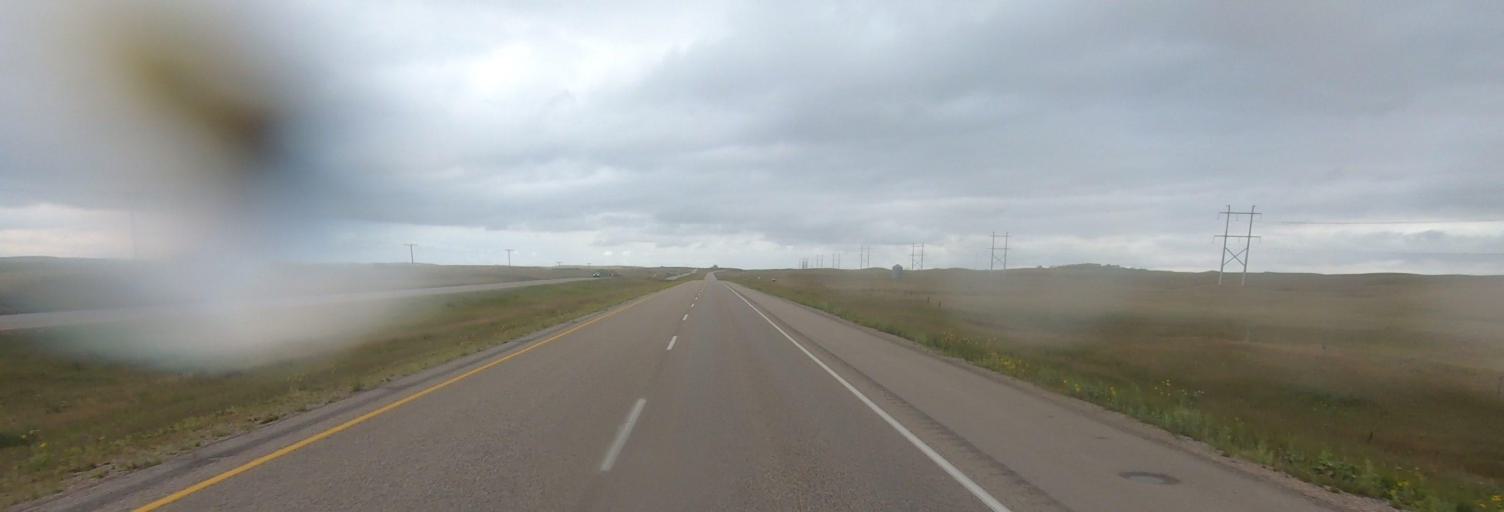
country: CA
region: Saskatchewan
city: Gravelbourg
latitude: 50.4631
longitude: -106.4119
